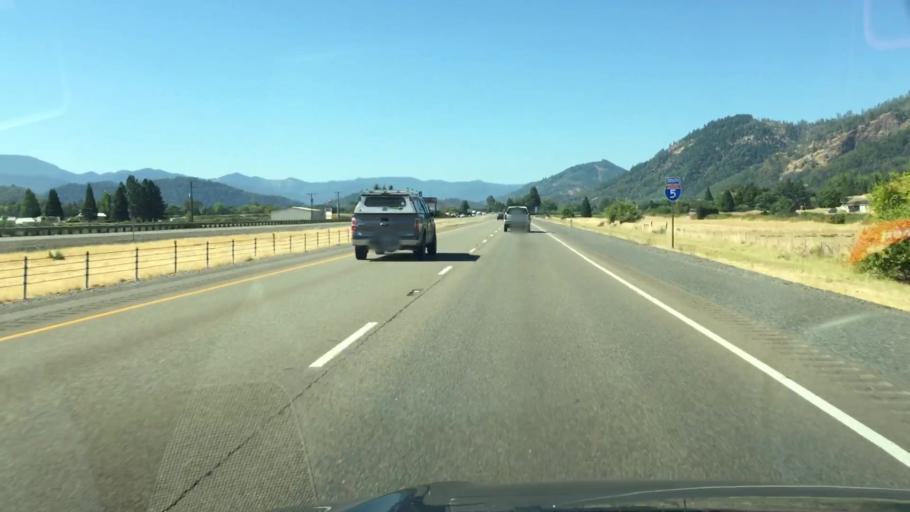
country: US
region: Oregon
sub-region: Douglas County
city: Tri-City
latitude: 43.0020
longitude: -123.3145
